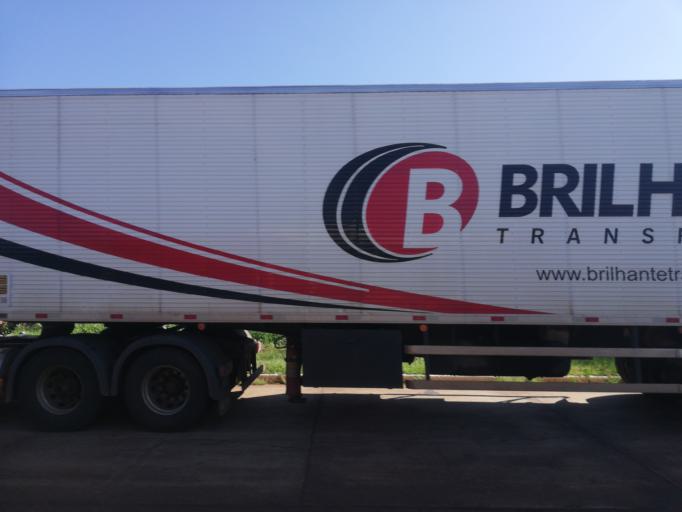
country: AR
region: Misiones
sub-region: Departamento de Iguazu
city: Puerto Iguazu
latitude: -25.5781
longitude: -54.5572
